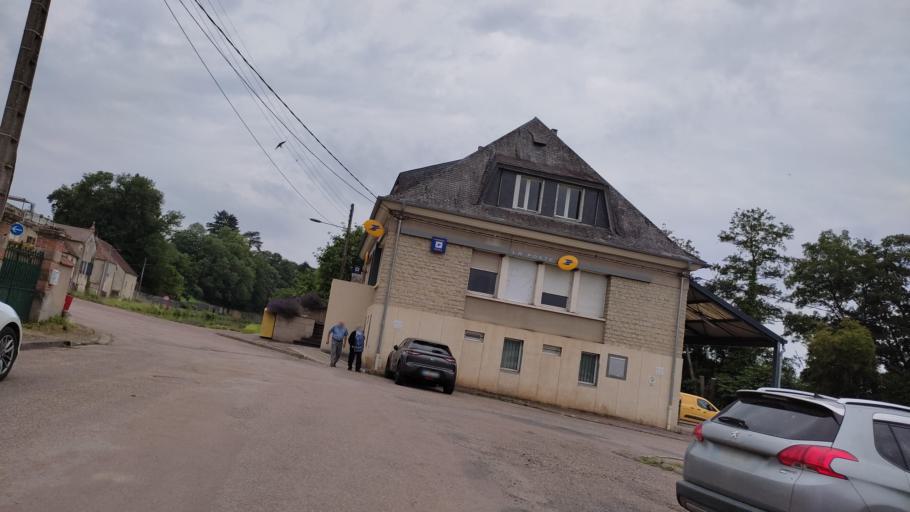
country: FR
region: Bourgogne
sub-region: Departement de la Nievre
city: Chatillon-en-Bazois
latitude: 47.0520
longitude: 3.6537
